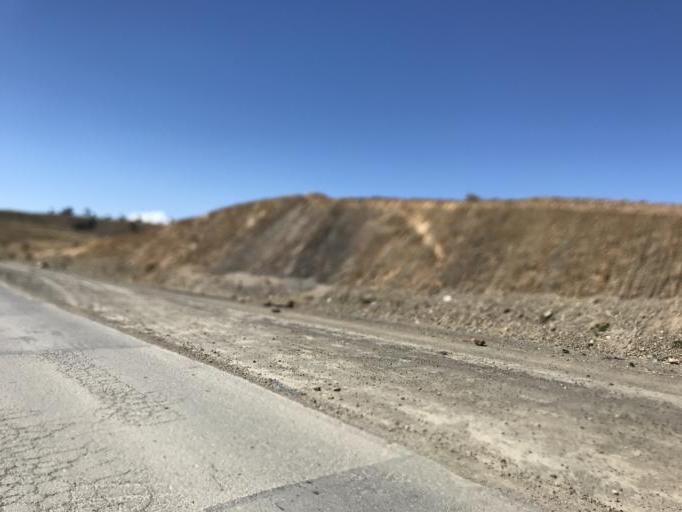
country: BO
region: La Paz
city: Huarina
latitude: -16.2005
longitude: -68.6314
